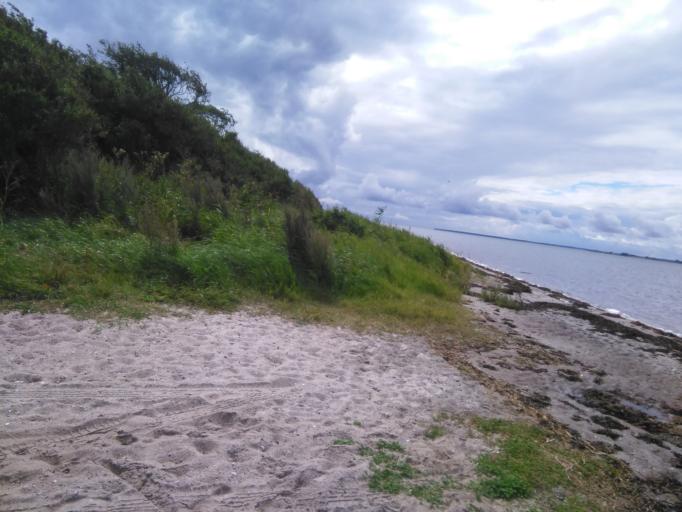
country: DK
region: Central Jutland
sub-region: Odder Kommune
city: Odder
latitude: 55.8619
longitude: 10.1393
